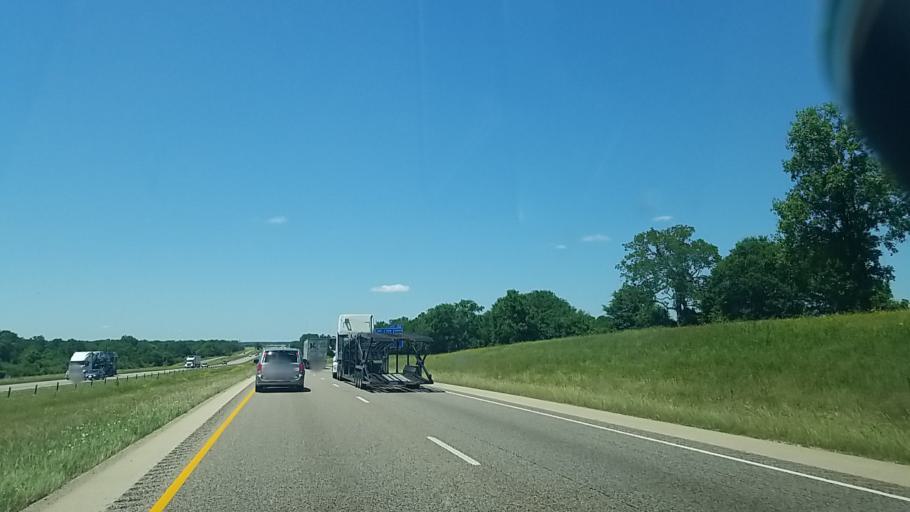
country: US
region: Texas
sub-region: Madison County
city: Madisonville
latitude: 31.0777
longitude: -95.9559
